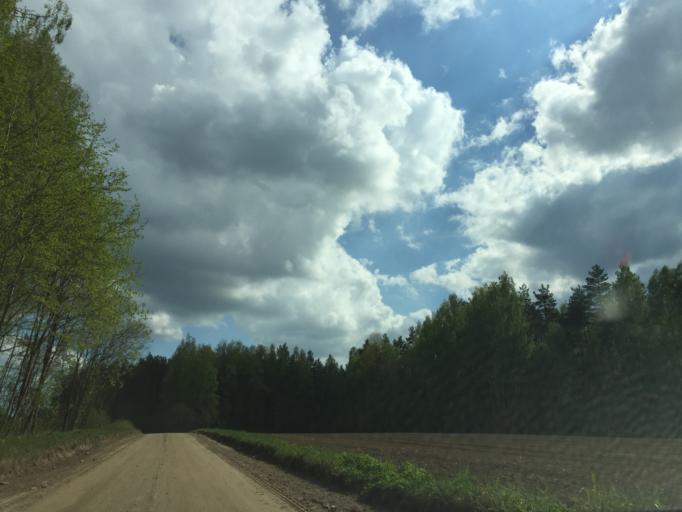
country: LV
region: Pargaujas
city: Stalbe
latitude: 57.3176
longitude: 24.8771
